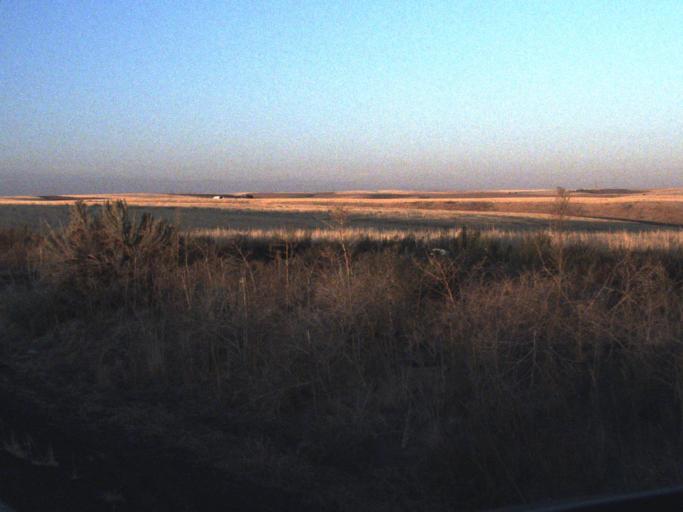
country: US
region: Washington
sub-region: Adams County
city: Ritzville
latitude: 47.0168
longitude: -118.6636
